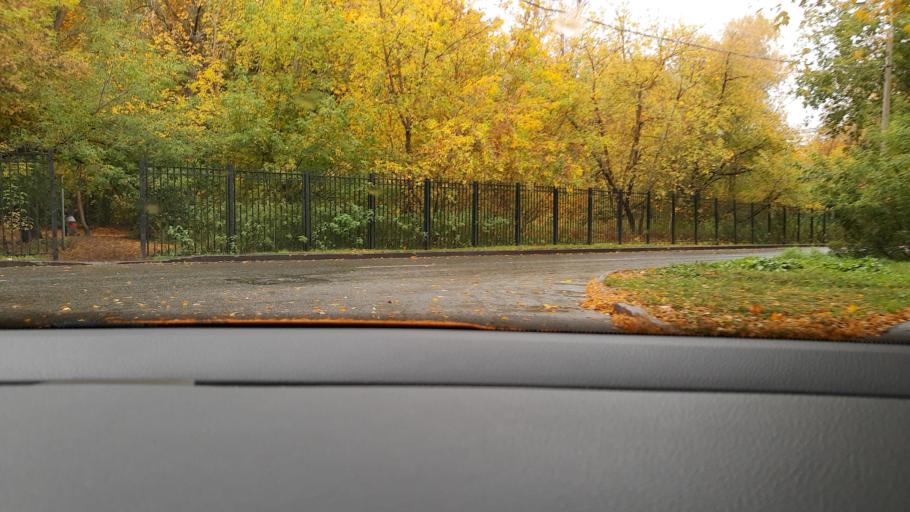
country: RU
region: Moscow
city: Gol'yanovo
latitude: 55.7993
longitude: 37.8269
